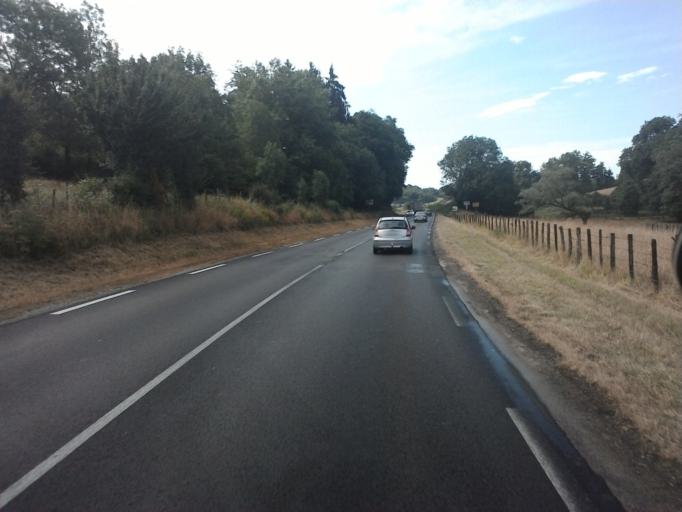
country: FR
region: Franche-Comte
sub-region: Departement du Jura
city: Lons-le-Saunier
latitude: 46.7022
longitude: 5.5547
